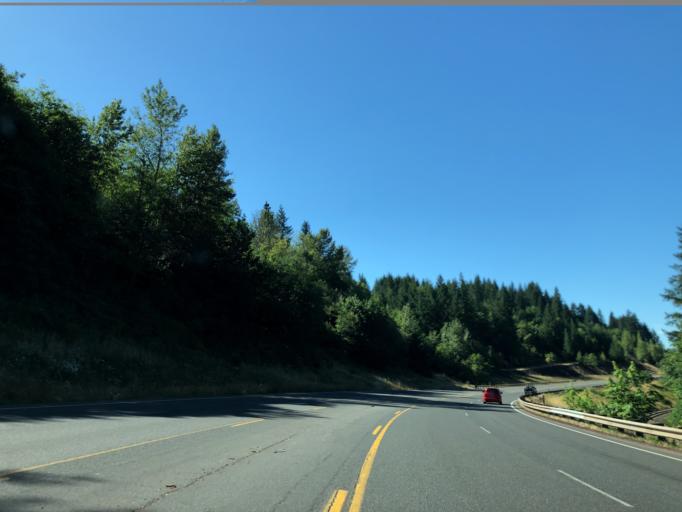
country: US
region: Oregon
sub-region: Linn County
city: Sweet Home
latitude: 44.4059
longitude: -122.7623
